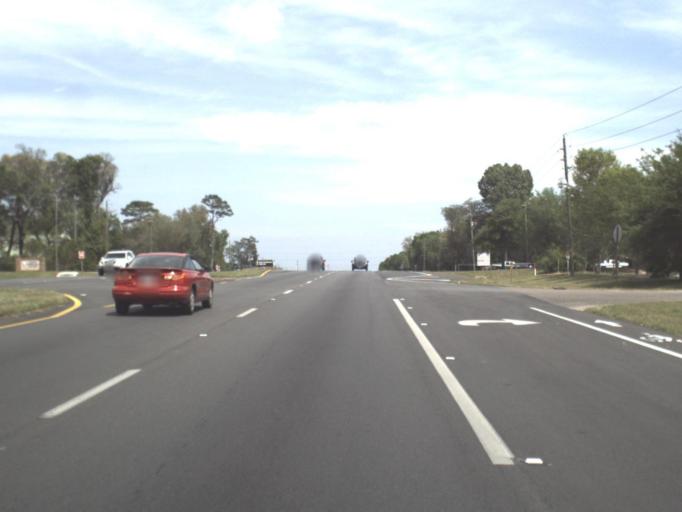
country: US
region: Florida
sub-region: Escambia County
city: Ensley
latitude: 30.5325
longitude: -87.2441
